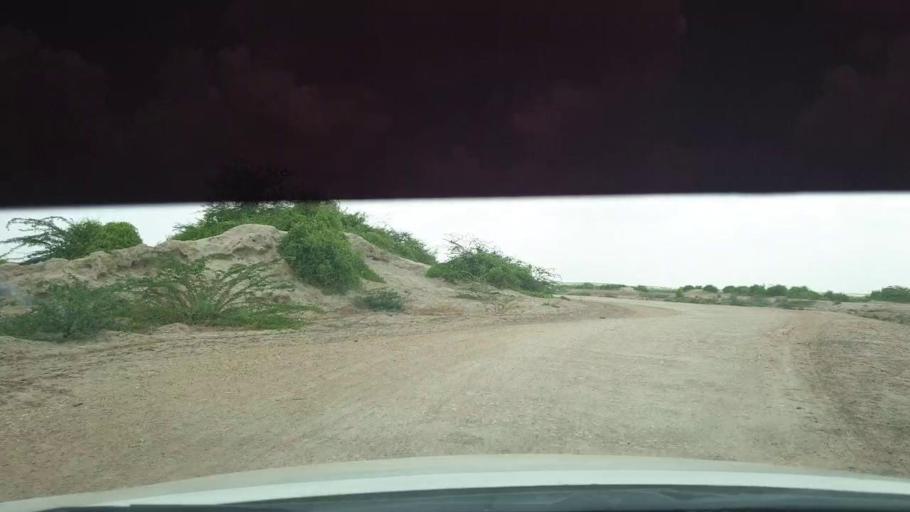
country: PK
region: Sindh
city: Kadhan
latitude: 24.4765
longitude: 69.0641
